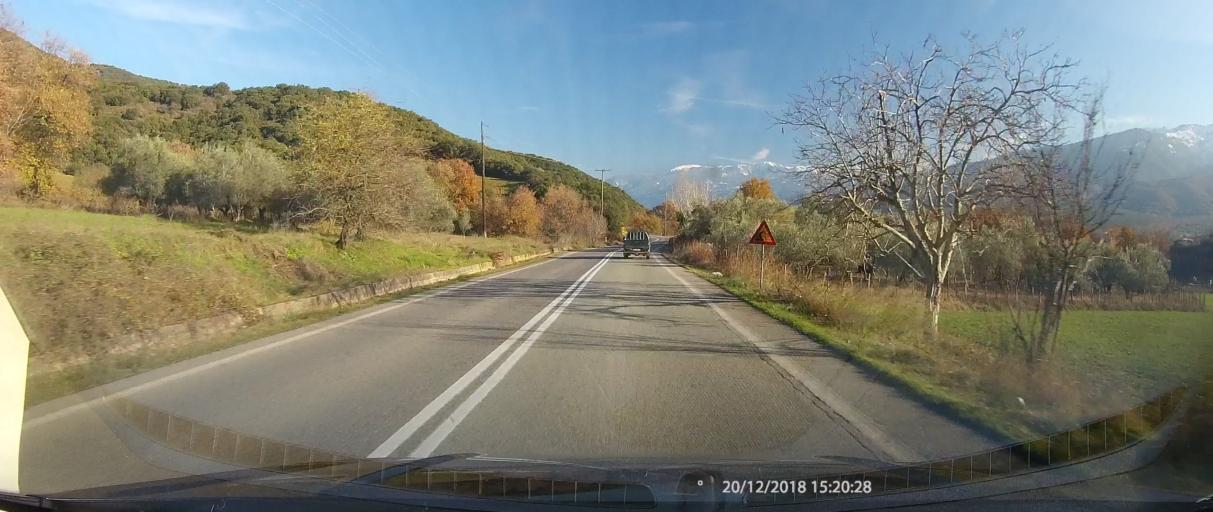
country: GR
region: Central Greece
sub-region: Nomos Fthiotidos
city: Makrakomi
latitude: 38.9355
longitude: 22.0579
